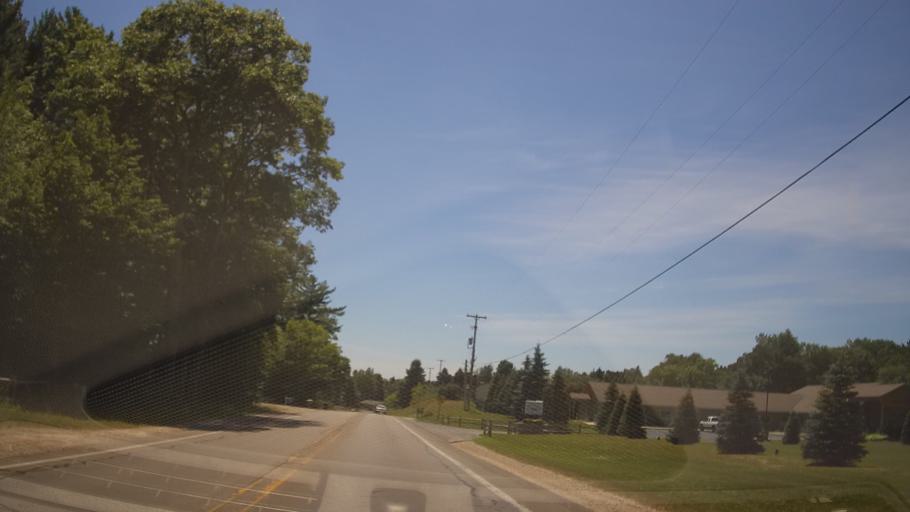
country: US
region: Michigan
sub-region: Grand Traverse County
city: Traverse City
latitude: 44.7125
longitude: -85.6899
